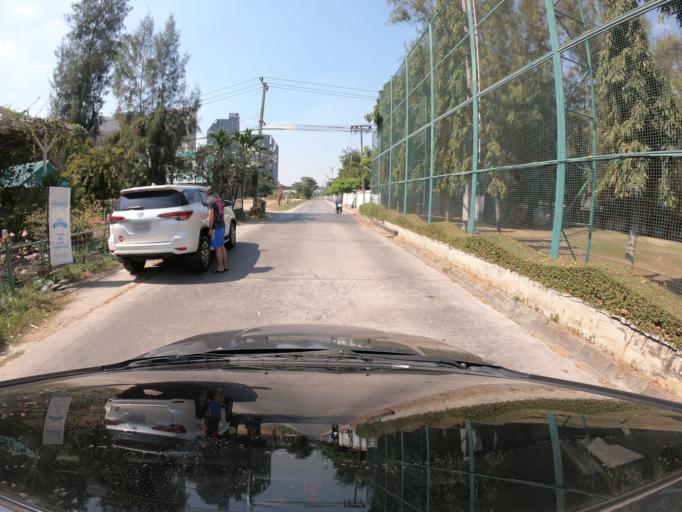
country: TH
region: Bangkok
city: Bang Na
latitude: 13.6654
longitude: 100.6076
